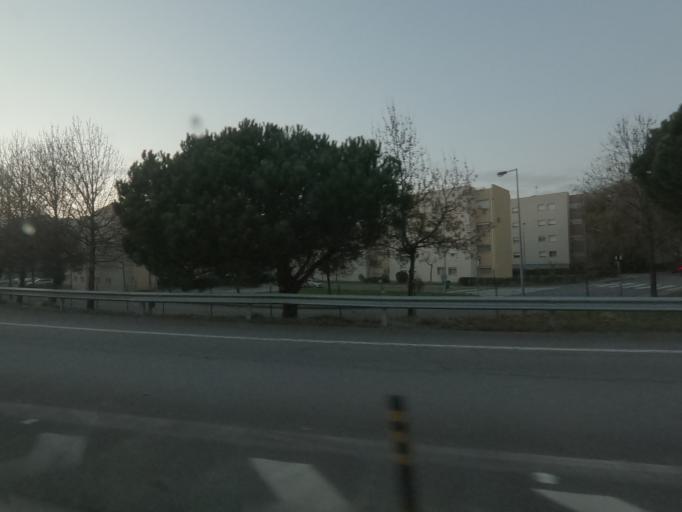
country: PT
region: Porto
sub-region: Porto
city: Porto
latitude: 41.1750
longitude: -8.6227
